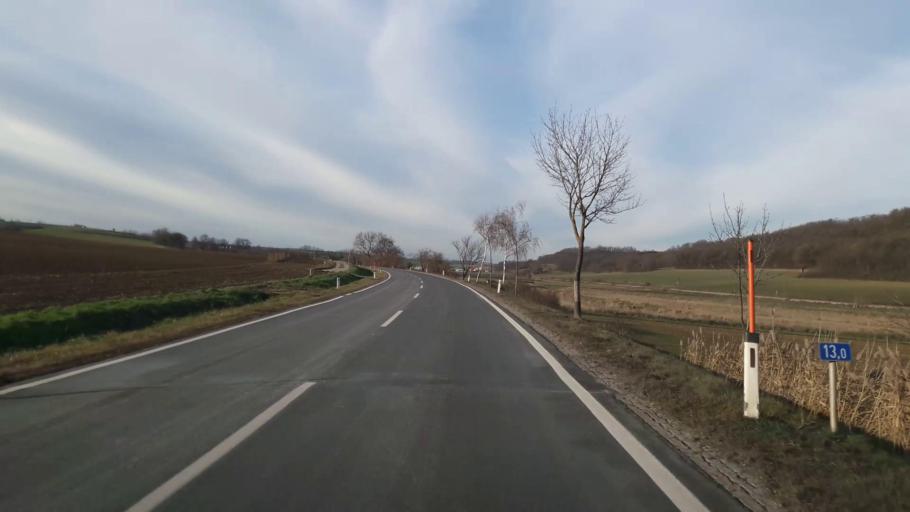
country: AT
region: Lower Austria
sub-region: Politischer Bezirk Ganserndorf
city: Gross-Schweinbarth
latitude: 48.4247
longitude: 16.6242
